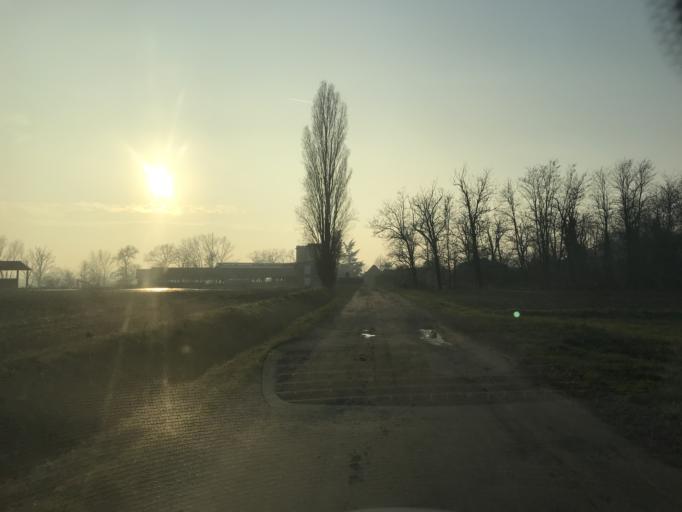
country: IT
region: Lombardy
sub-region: Provincia di Lodi
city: Bargano
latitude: 45.2384
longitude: 9.4441
